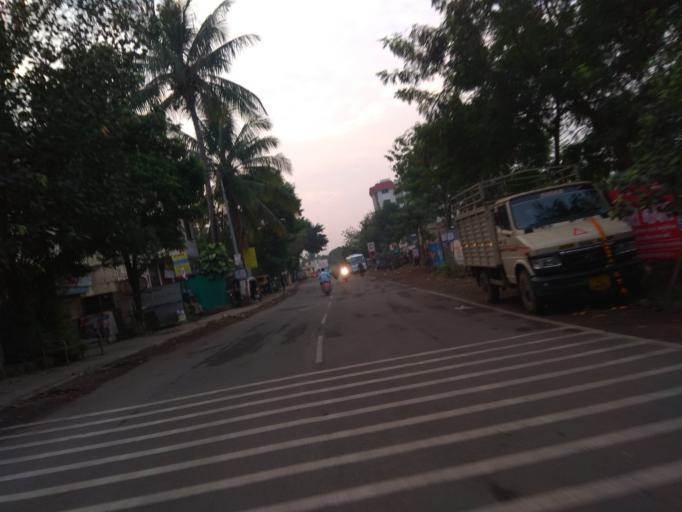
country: IN
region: Maharashtra
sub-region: Pune Division
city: Kharakvasla
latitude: 18.4830
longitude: 73.8047
